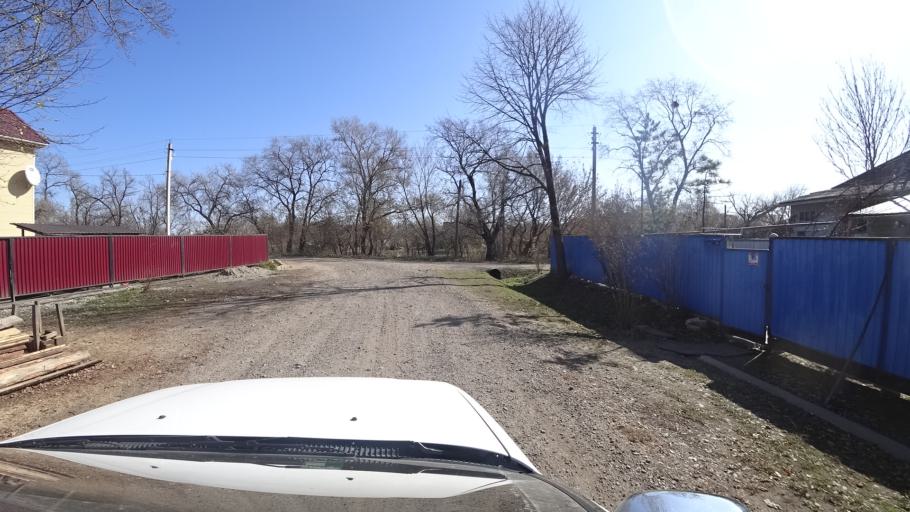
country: RU
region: Primorskiy
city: Dal'nerechensk
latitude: 45.9101
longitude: 133.7949
